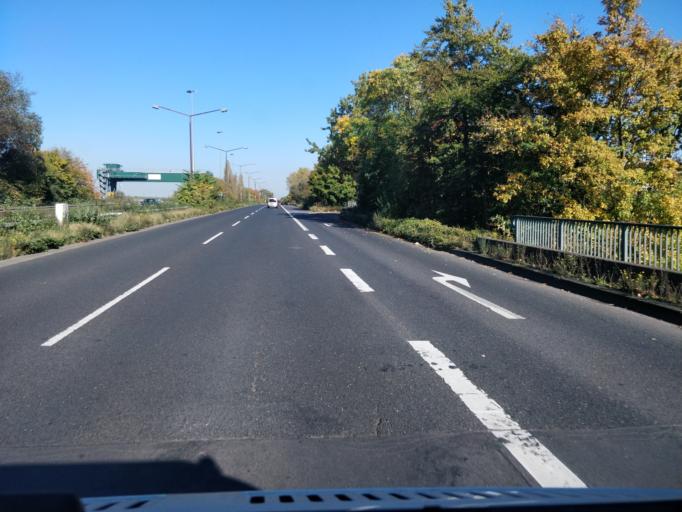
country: DE
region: North Rhine-Westphalia
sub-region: Regierungsbezirk Koln
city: Bilderstoeckchen
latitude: 51.0027
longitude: 6.9473
